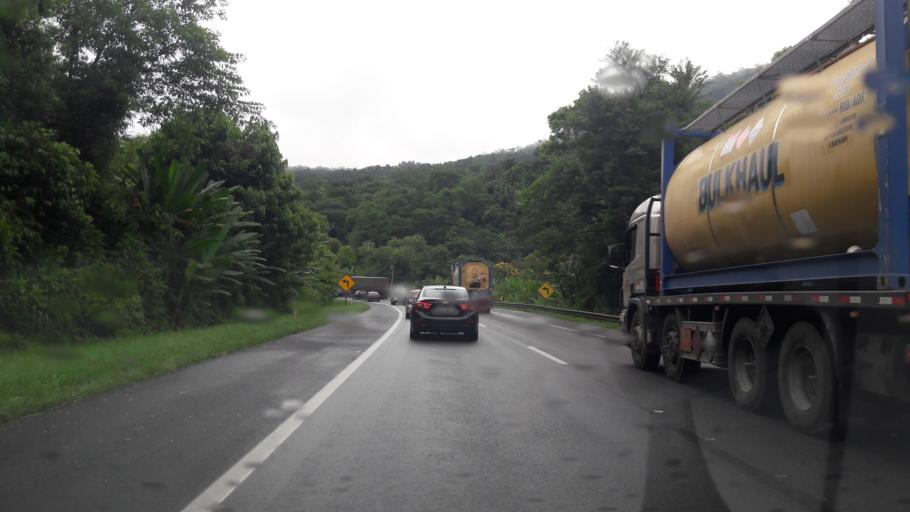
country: BR
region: Parana
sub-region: Antonina
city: Antonina
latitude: -25.5608
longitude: -48.8160
